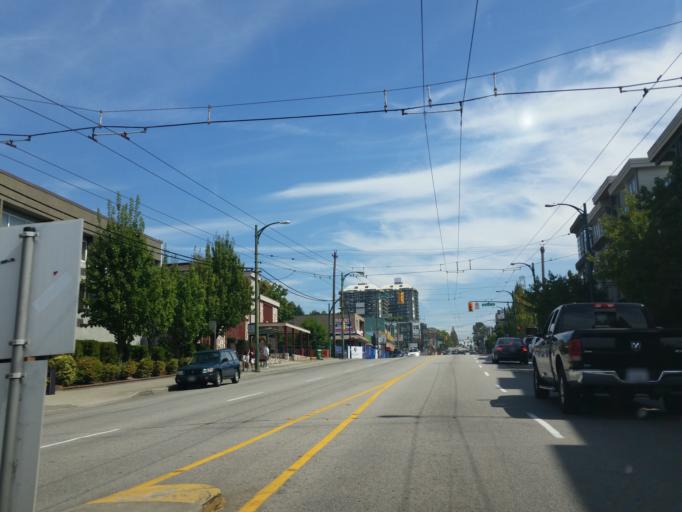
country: CA
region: British Columbia
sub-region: Fraser Valley Regional District
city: North Vancouver
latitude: 49.2811
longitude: -123.0296
